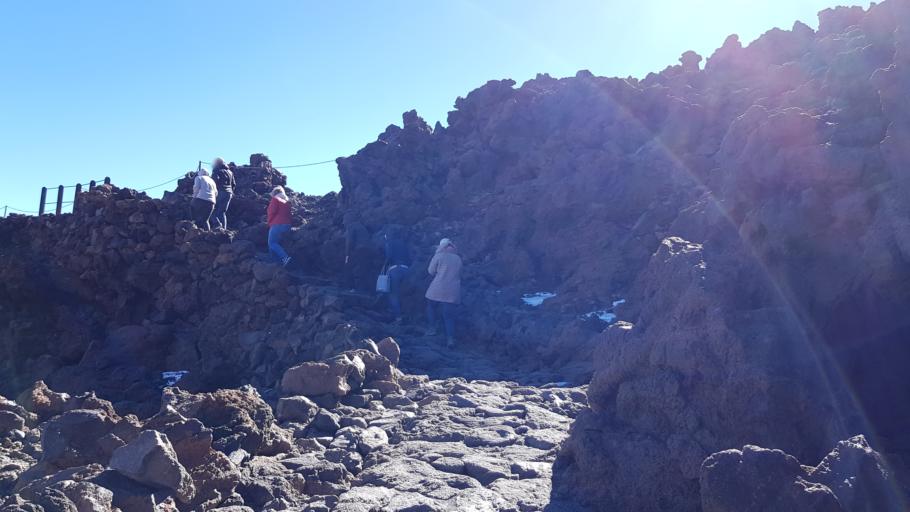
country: ES
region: Canary Islands
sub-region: Provincia de Santa Cruz de Tenerife
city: La Guancha
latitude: 28.2708
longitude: -16.6392
